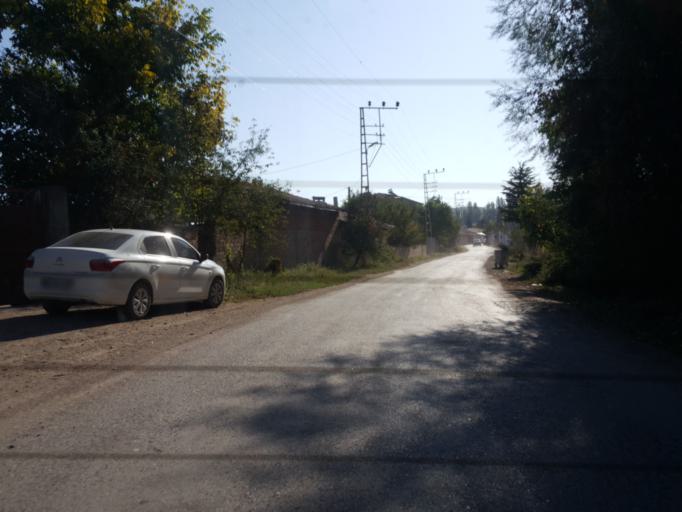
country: TR
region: Amasya
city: Saribugday
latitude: 40.7494
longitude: 35.4574
